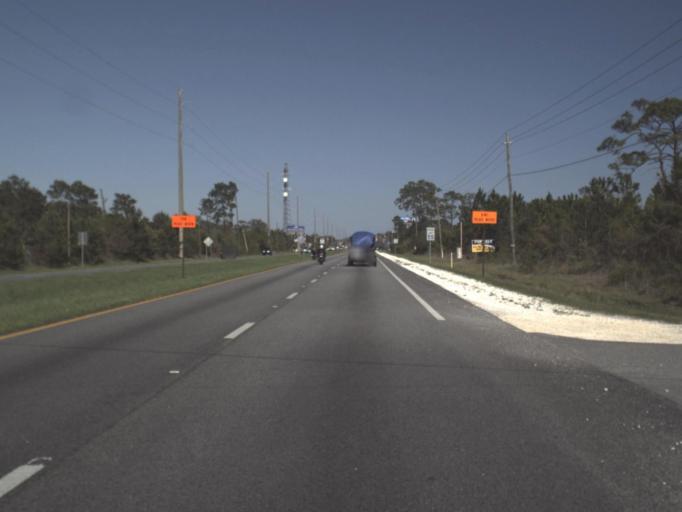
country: US
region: Florida
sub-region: Santa Rosa County
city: Navarre
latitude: 30.4098
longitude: -86.7959
